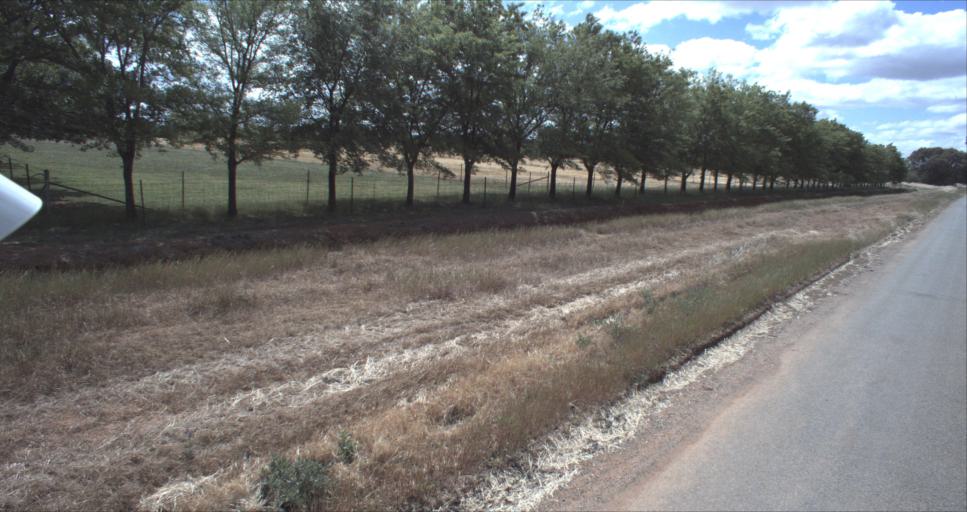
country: AU
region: New South Wales
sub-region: Leeton
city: Leeton
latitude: -34.5889
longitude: 146.3955
